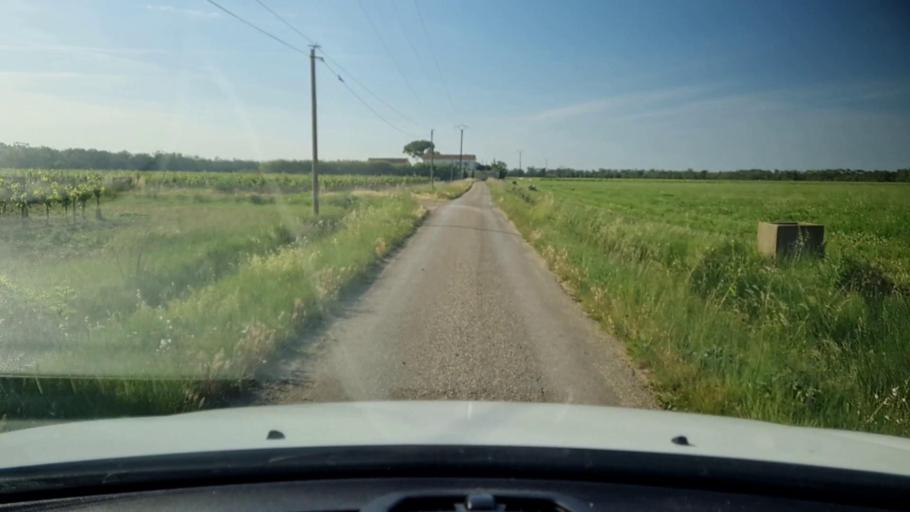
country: FR
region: Languedoc-Roussillon
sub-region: Departement du Gard
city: Le Cailar
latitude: 43.6409
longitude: 4.2291
